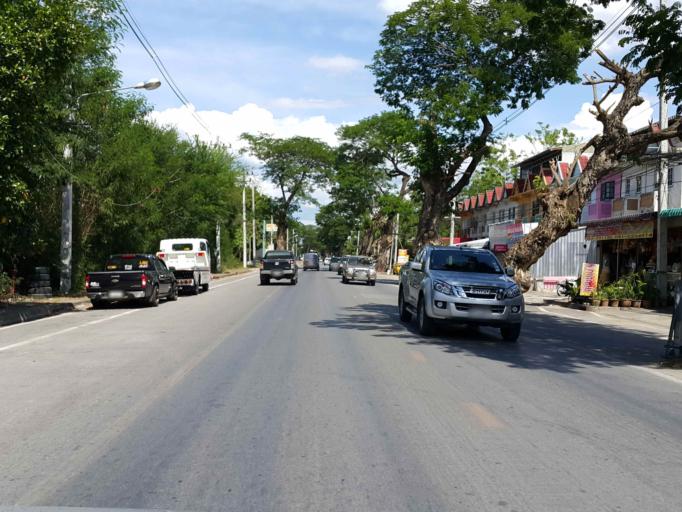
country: TH
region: Chiang Mai
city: San Kamphaeng
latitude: 18.7586
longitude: 99.0916
